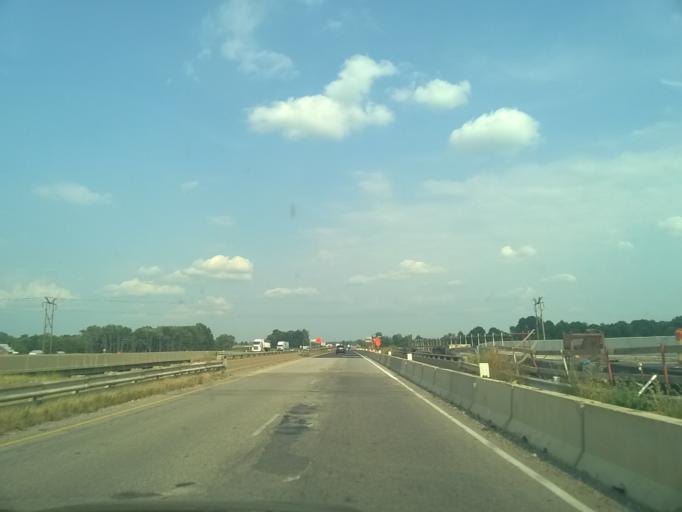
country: US
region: Indiana
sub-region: Vigo County
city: Terre Haute
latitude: 39.4305
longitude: -87.3324
